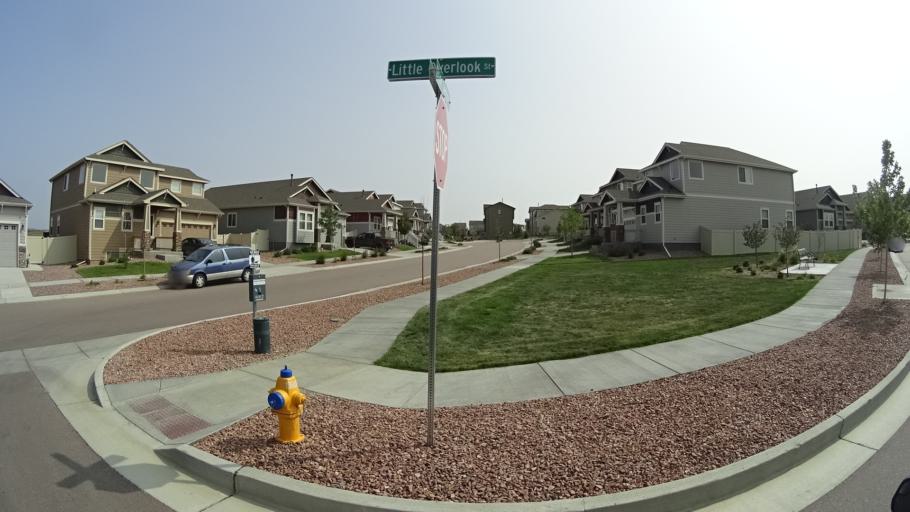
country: US
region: Colorado
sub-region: El Paso County
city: Stratmoor
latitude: 38.8094
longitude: -104.7901
